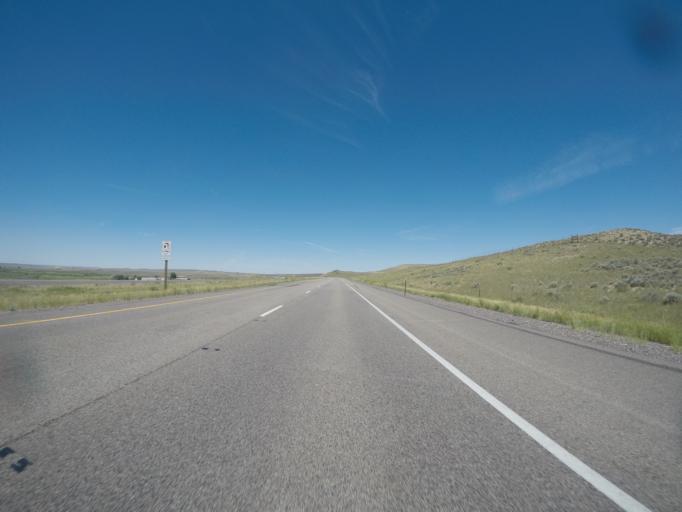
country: US
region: Wyoming
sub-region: Carbon County
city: Saratoga
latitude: 41.7422
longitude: -106.7649
